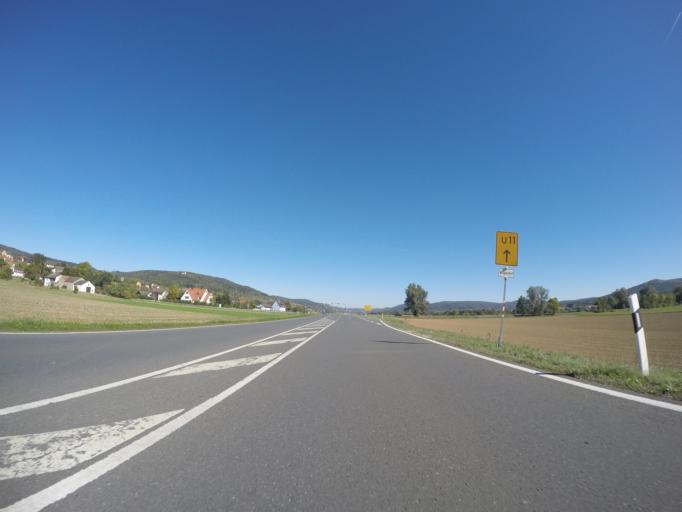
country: DE
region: Bavaria
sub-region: Upper Franconia
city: Kirchehrenbach
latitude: 49.7391
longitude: 11.1334
